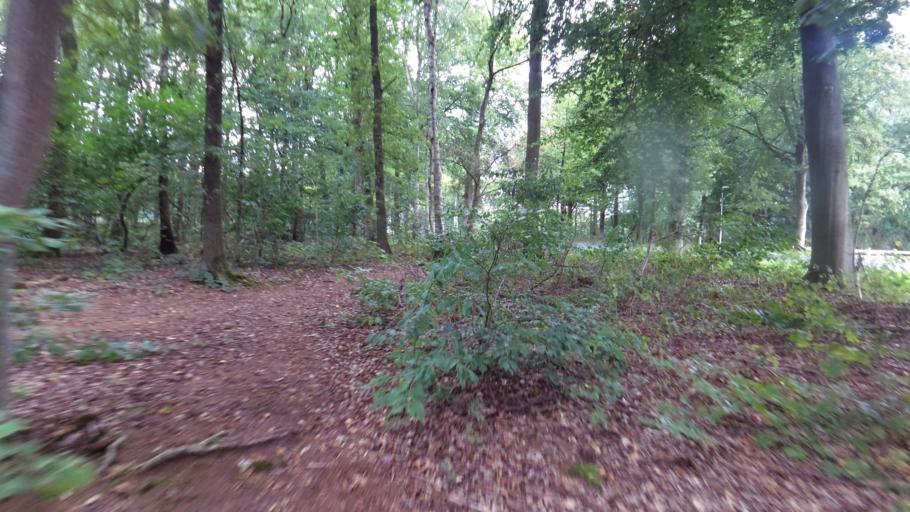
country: NL
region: Gelderland
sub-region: Gemeente Renkum
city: Renkum
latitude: 51.9901
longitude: 5.7289
